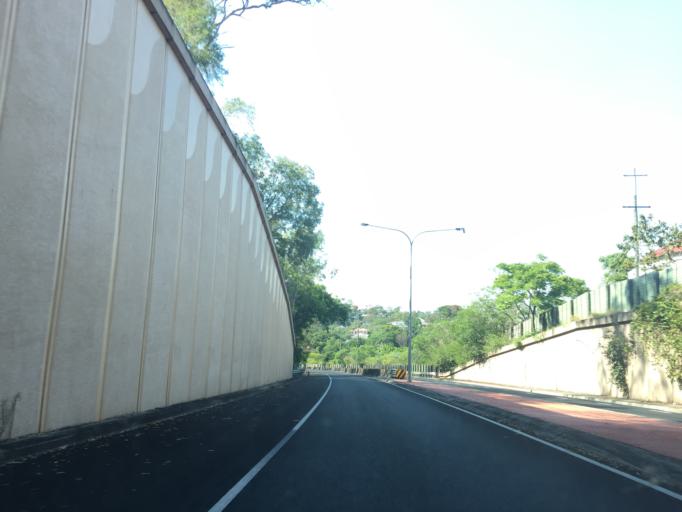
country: AU
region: Queensland
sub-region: Brisbane
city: Milton
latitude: -27.4613
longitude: 152.9883
